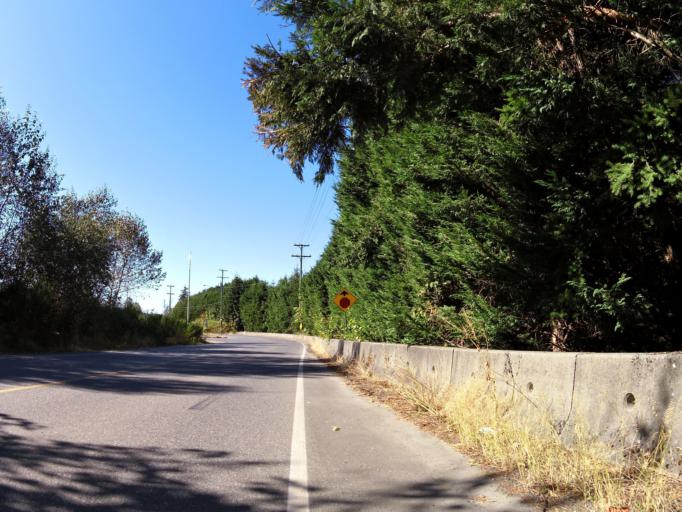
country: CA
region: British Columbia
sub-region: Cowichan Valley Regional District
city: Ladysmith
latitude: 49.0114
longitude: -123.8396
